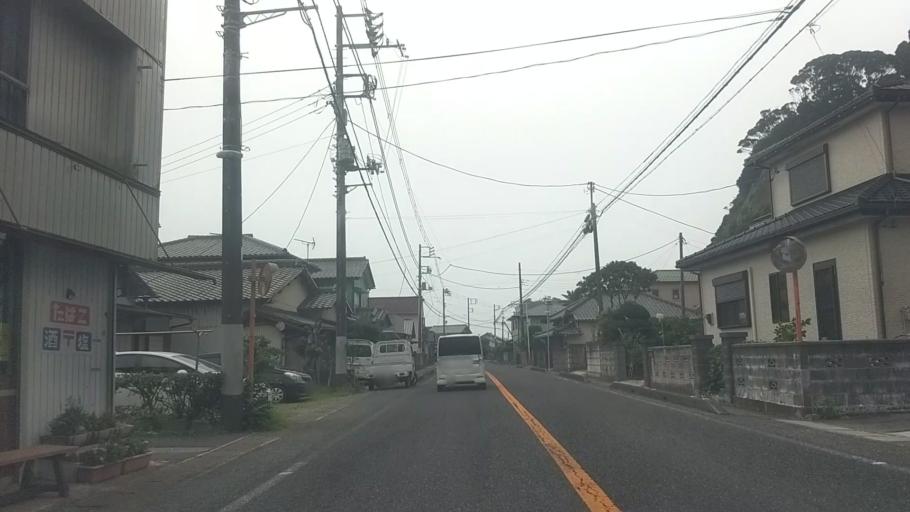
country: JP
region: Chiba
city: Katsuura
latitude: 35.1810
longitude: 140.3478
